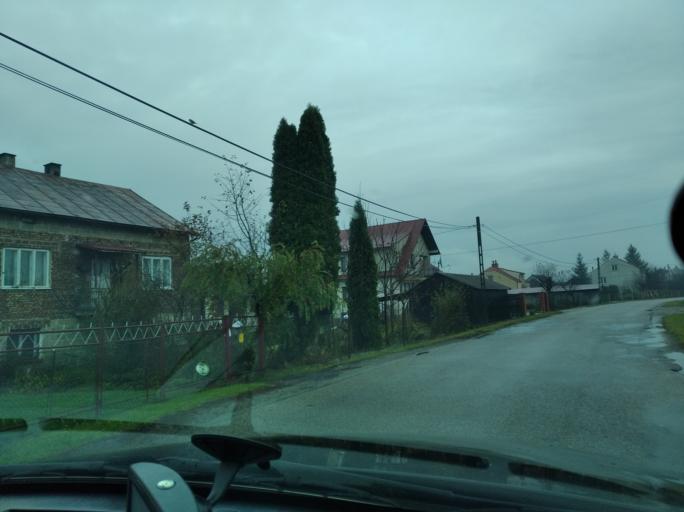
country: PL
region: Subcarpathian Voivodeship
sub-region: Powiat strzyzowski
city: Czudec
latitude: 49.9301
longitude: 21.8498
